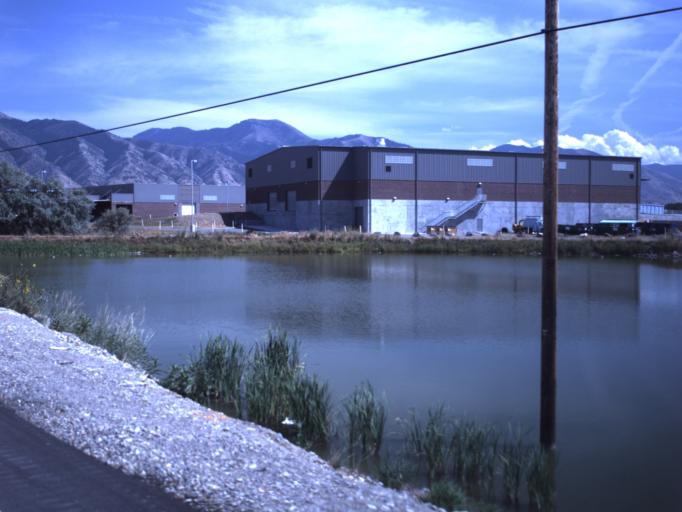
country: US
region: Utah
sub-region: Cache County
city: Logan
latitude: 41.7358
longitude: -111.8738
